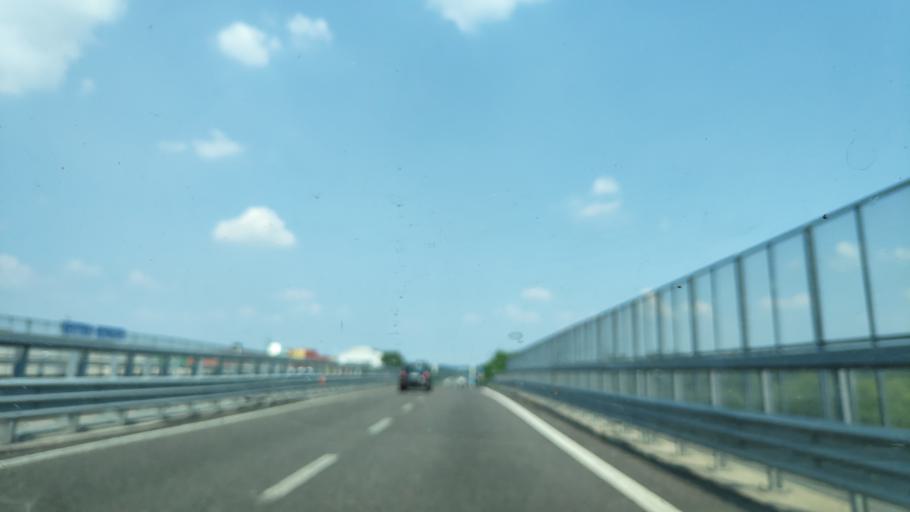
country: IT
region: Lombardy
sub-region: Citta metropolitana di Milano
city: San Bovio-San Felice
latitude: 45.4783
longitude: 9.3136
